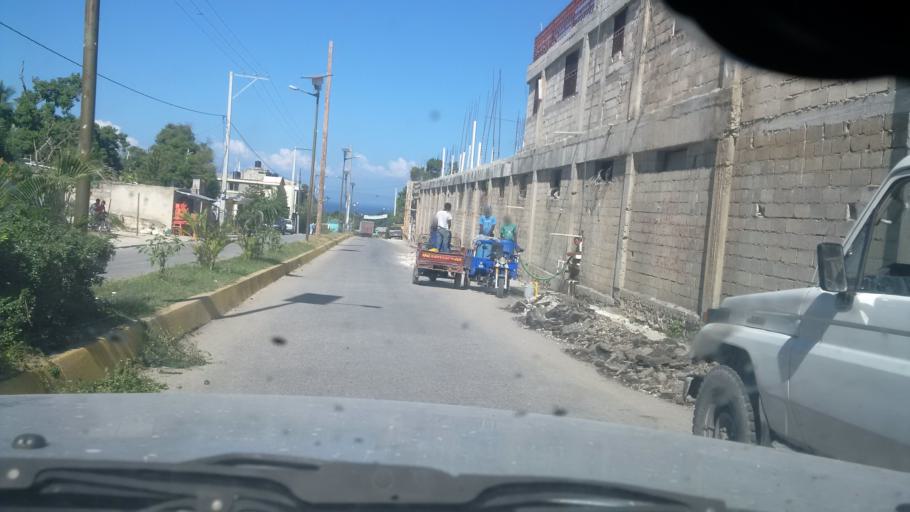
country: HT
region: Ouest
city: Tigwav
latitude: 18.4377
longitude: -72.8506
